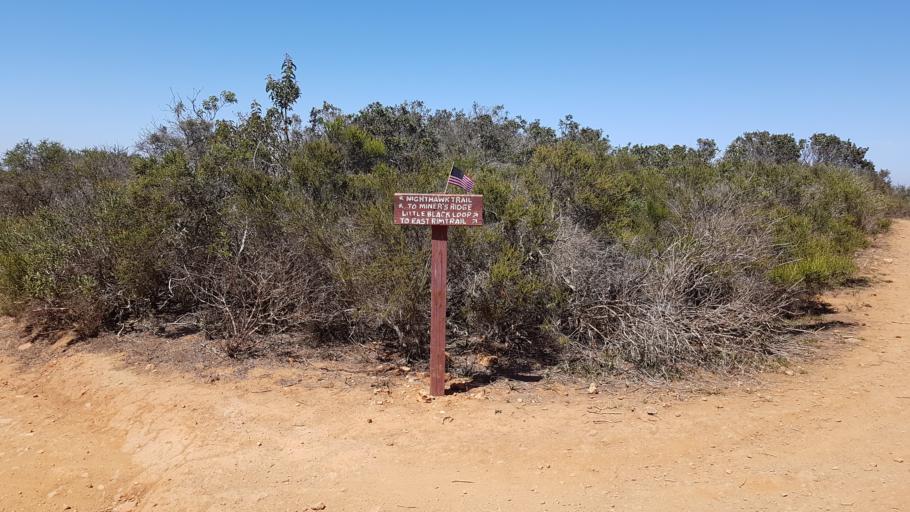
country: US
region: California
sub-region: San Diego County
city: Poway
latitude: 32.9816
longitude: -117.1108
